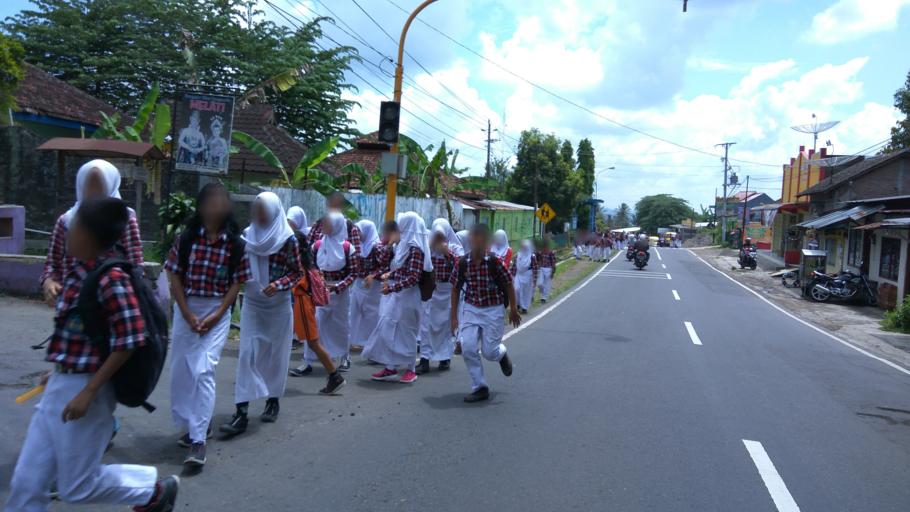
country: ID
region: Central Java
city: Ambarawa
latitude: -7.2438
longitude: 110.3943
